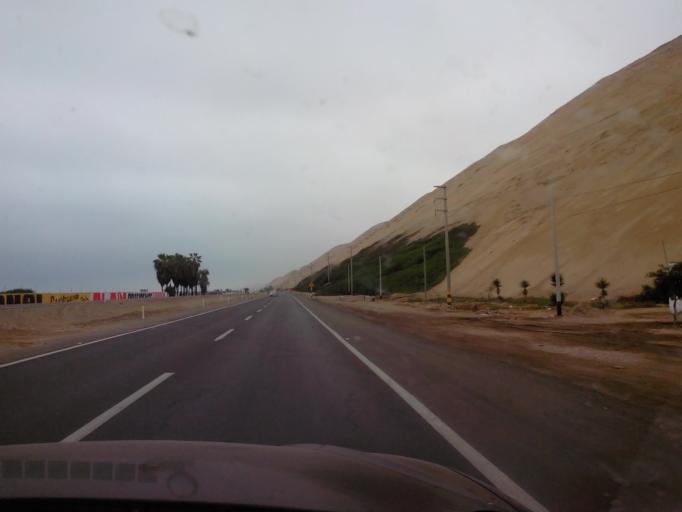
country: PE
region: Ica
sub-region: Provincia de Chincha
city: San Pedro
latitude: -13.3475
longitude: -76.2255
